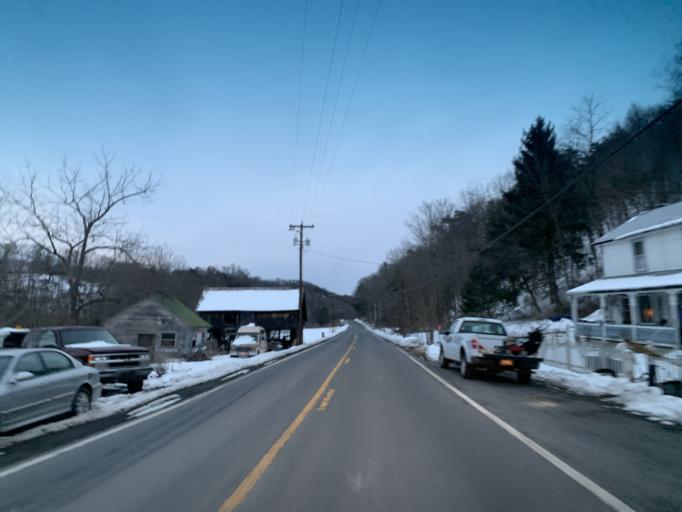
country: US
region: Maryland
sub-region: Allegany County
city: Cumberland
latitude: 39.6899
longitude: -78.5051
